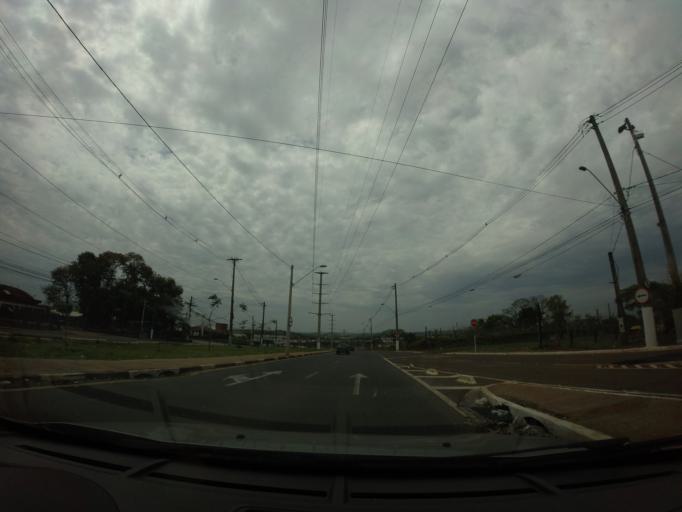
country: BR
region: Sao Paulo
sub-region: Hortolandia
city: Hortolandia
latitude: -22.8425
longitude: -47.1489
